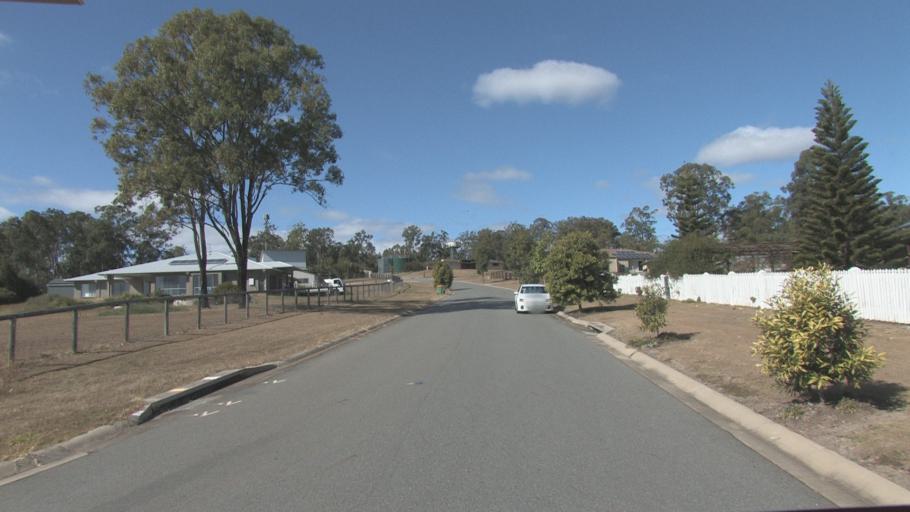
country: AU
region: Queensland
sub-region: Logan
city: Cedar Vale
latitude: -27.8912
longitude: 152.9995
